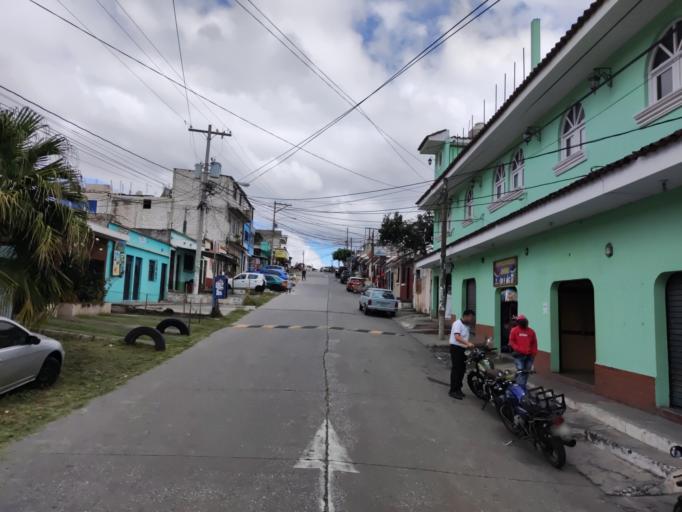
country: GT
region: Guatemala
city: Mixco
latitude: 14.5843
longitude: -90.6079
